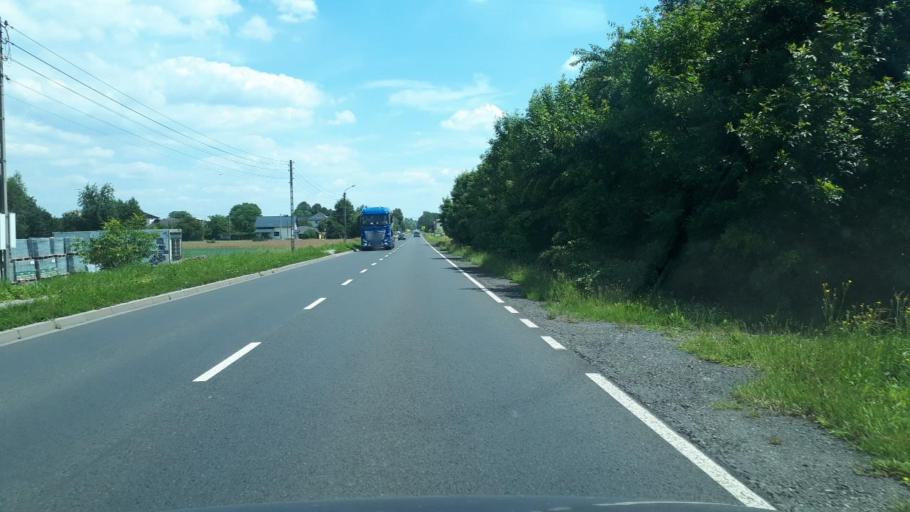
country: PL
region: Silesian Voivodeship
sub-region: Powiat pszczynski
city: Gora
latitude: 49.9717
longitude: 19.0932
